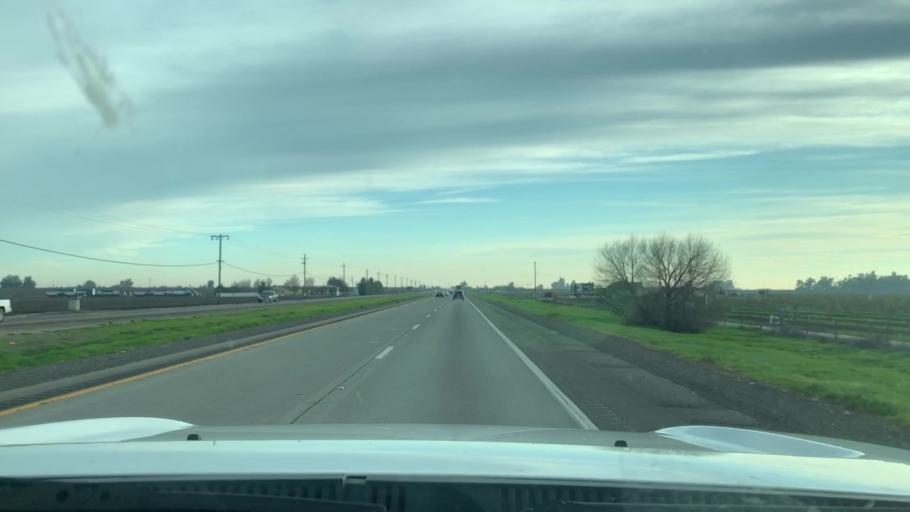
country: US
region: California
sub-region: Kings County
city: Lemoore
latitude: 36.3240
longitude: -119.8082
